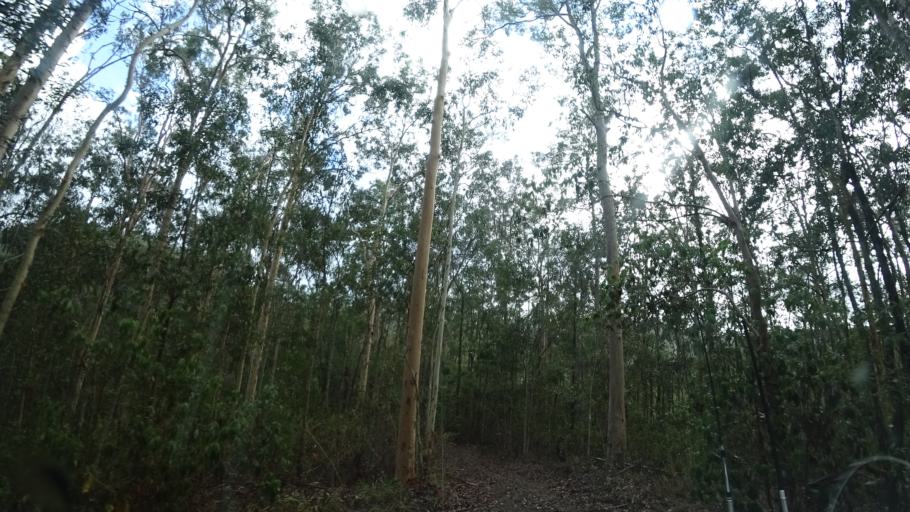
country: AU
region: Queensland
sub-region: Brisbane
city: Pullenvale
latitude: -27.4551
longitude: 152.8717
